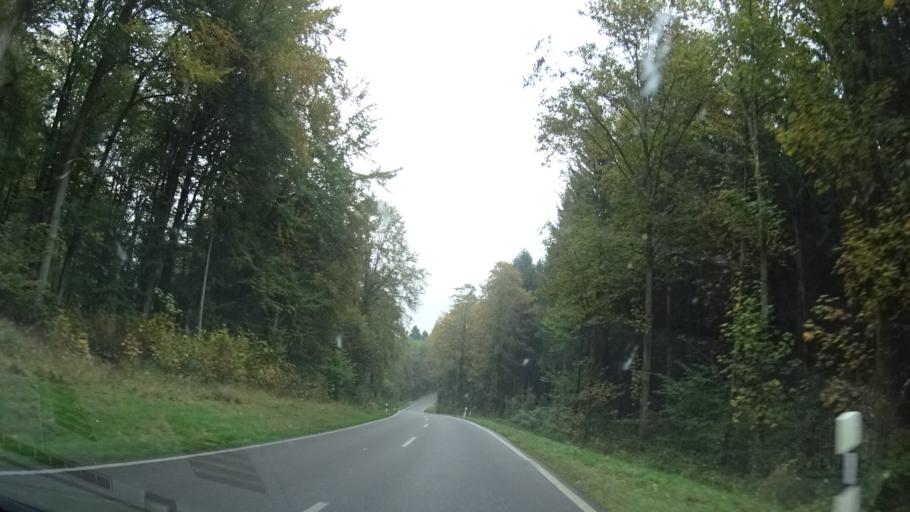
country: DE
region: Baden-Wuerttemberg
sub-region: Karlsruhe Region
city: Eisingen
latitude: 48.9968
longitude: 8.6588
